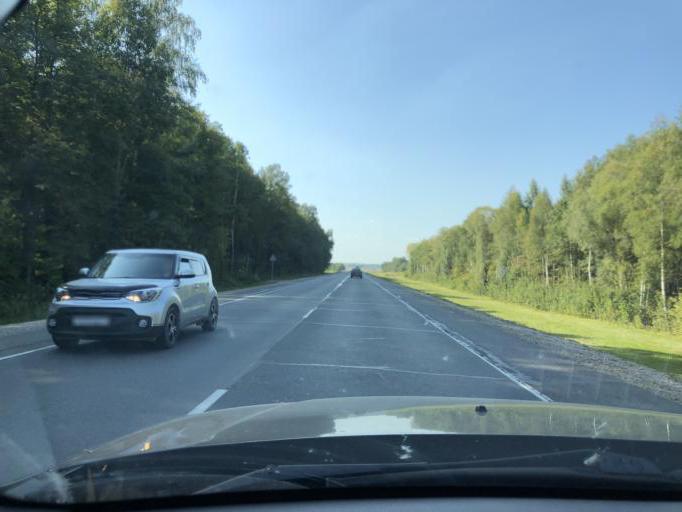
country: RU
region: Tula
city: Leninskiy
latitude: 54.2349
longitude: 37.3543
